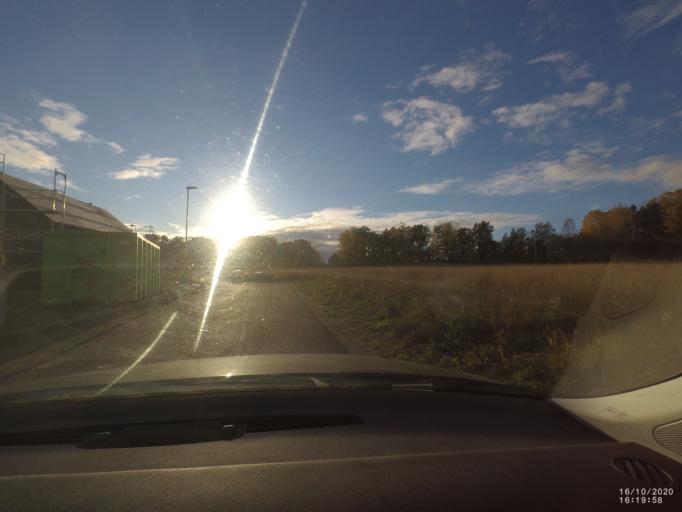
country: SE
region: Soedermanland
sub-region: Nykopings Kommun
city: Nykoping
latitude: 58.7745
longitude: 17.0080
